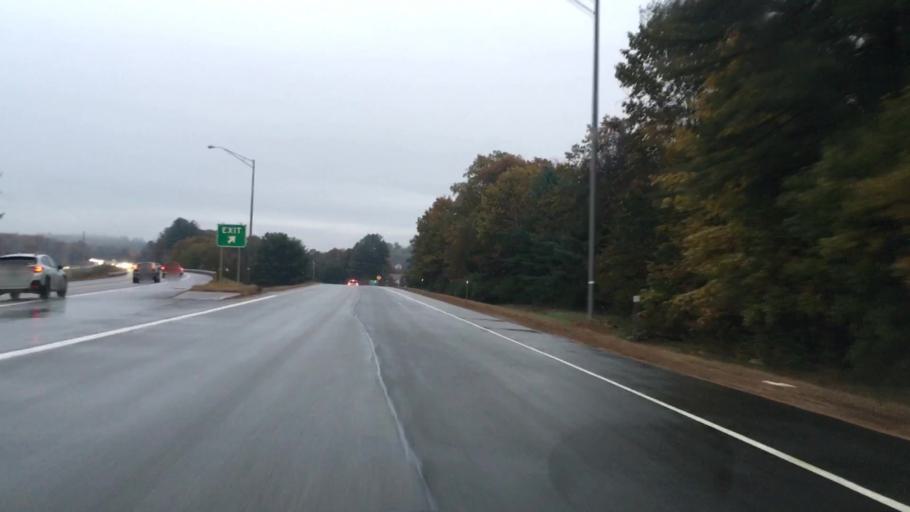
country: US
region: New Hampshire
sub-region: Hillsborough County
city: Milford
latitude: 42.8176
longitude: -71.6507
